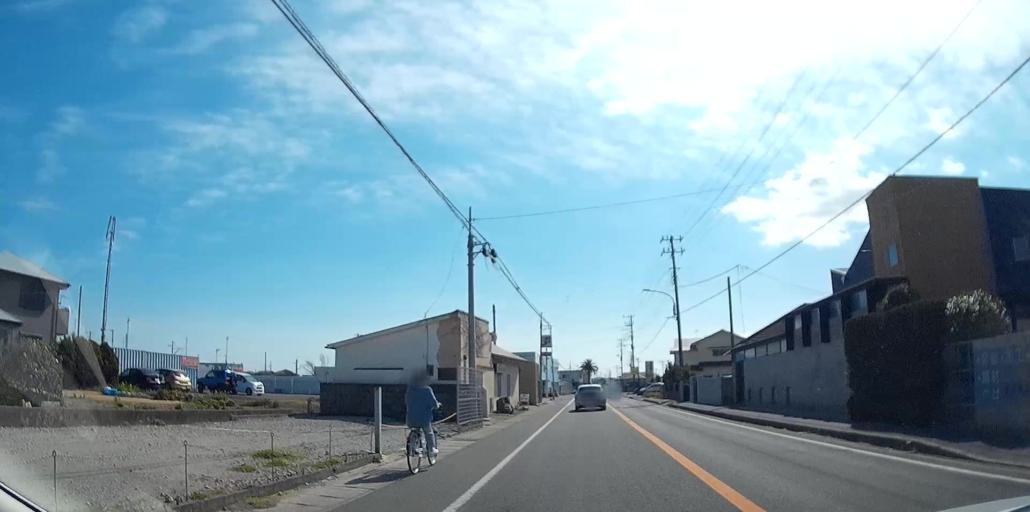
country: JP
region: Chiba
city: Tateyama
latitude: 35.0195
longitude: 139.8566
